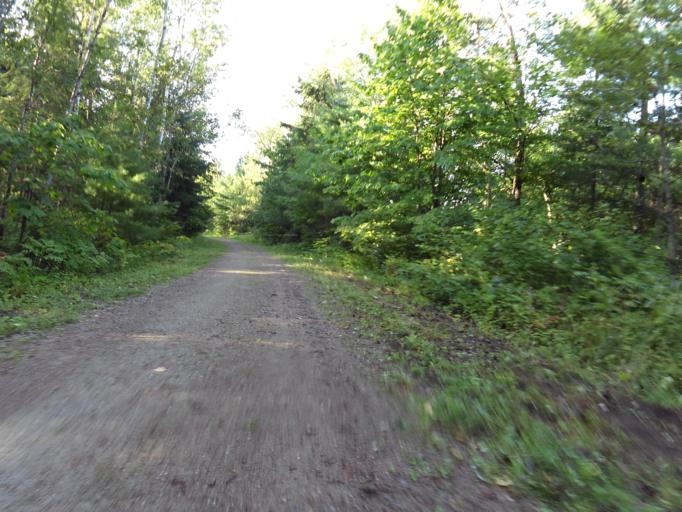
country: CA
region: Quebec
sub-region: Outaouais
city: Maniwaki
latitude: 46.2619
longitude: -76.0242
